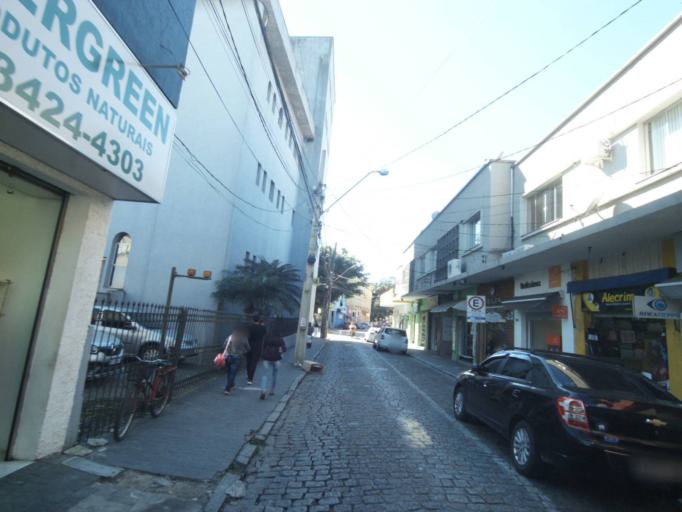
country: BR
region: Parana
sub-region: Paranagua
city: Paranagua
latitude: -25.5194
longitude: -48.5064
